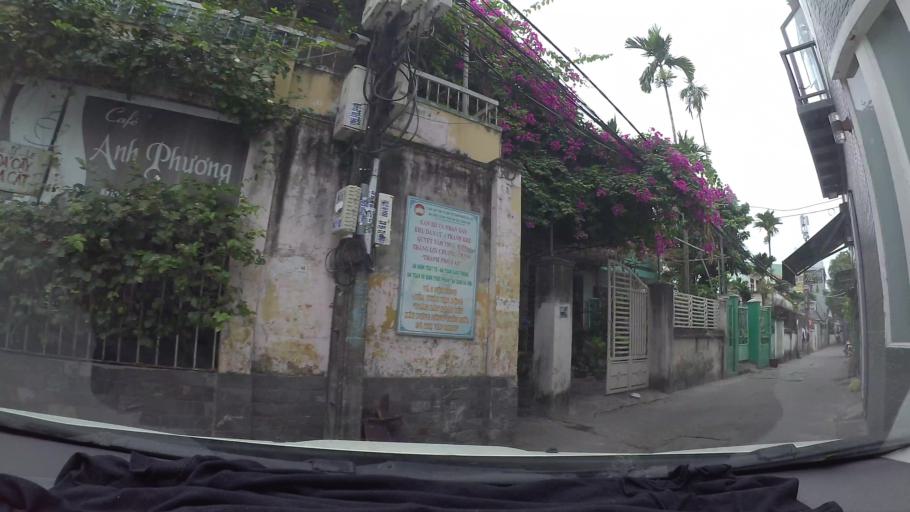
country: VN
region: Da Nang
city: Thanh Khe
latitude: 16.0642
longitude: 108.1870
